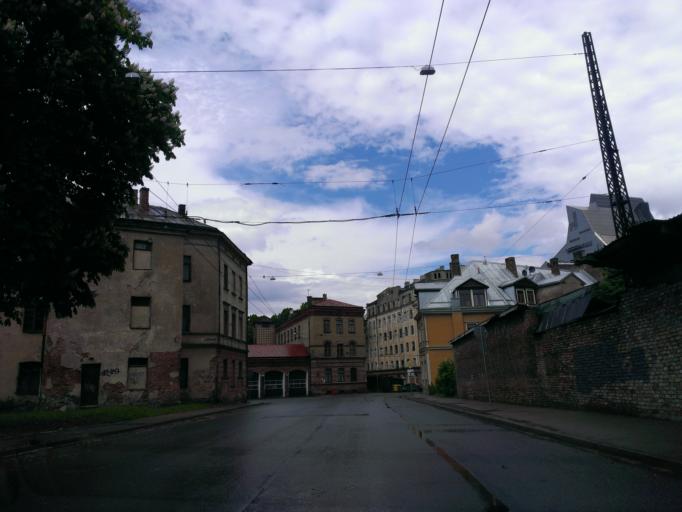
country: LV
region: Riga
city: Riga
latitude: 56.9388
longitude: 24.0968
